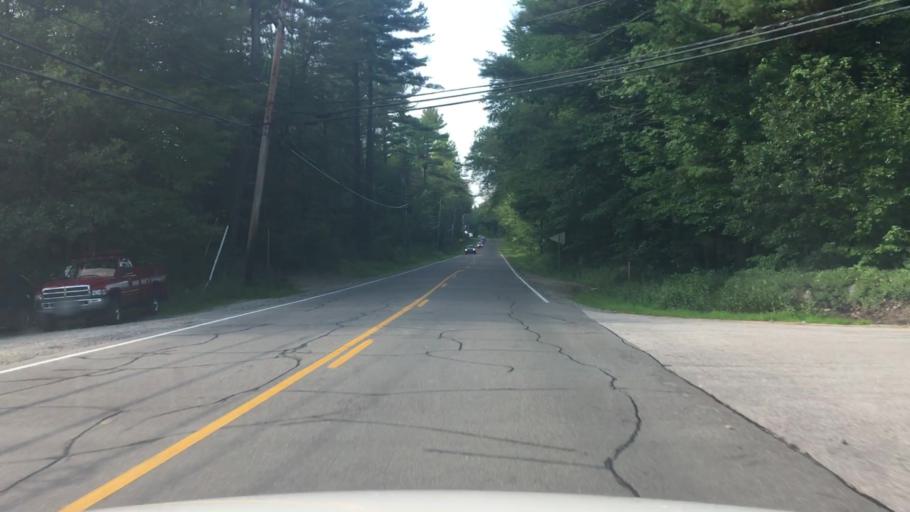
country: US
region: New Hampshire
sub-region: Rockingham County
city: Auburn
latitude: 42.9624
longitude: -71.3600
